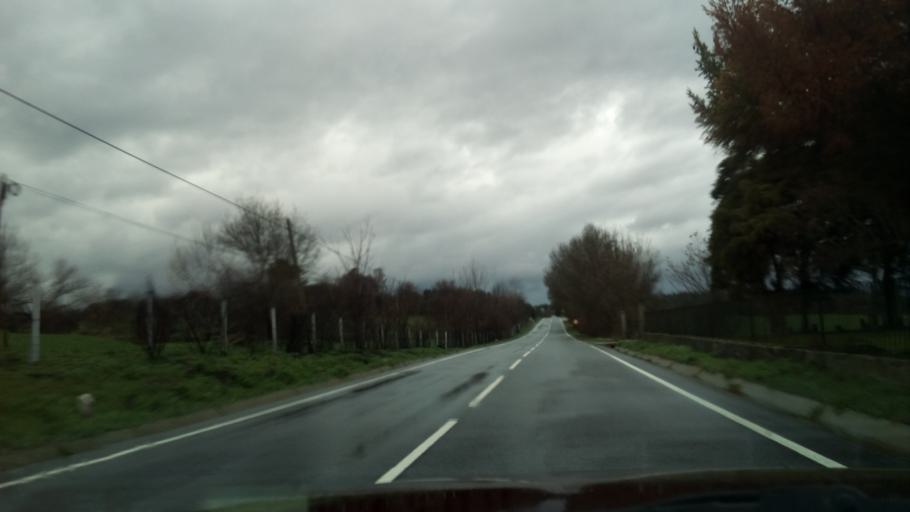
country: PT
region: Guarda
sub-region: Celorico da Beira
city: Celorico da Beira
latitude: 40.6213
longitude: -7.3161
